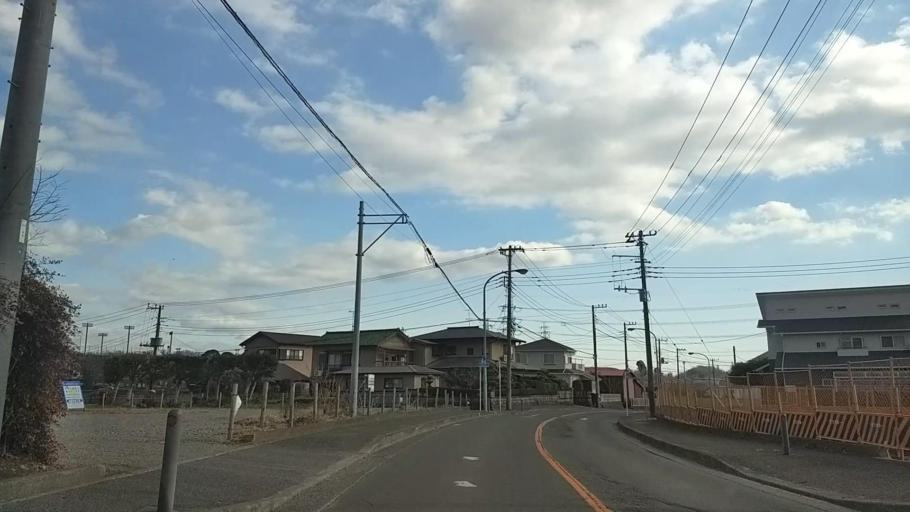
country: JP
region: Kanagawa
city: Isehara
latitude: 35.4193
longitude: 139.2976
